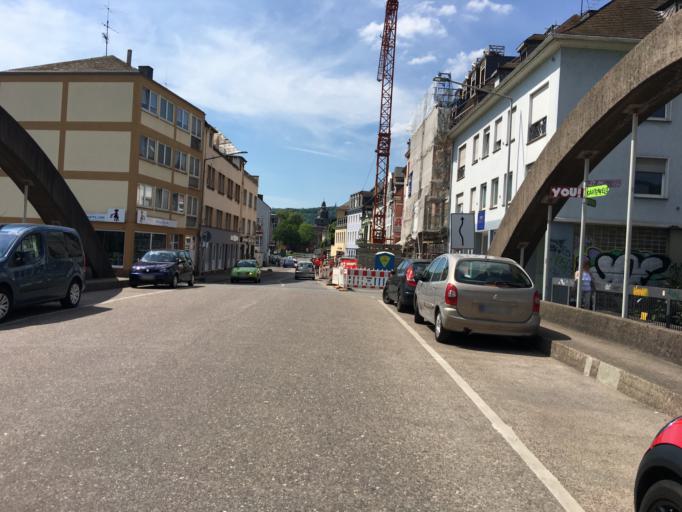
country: DE
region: Rheinland-Pfalz
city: Trier
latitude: 49.7532
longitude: 6.6489
